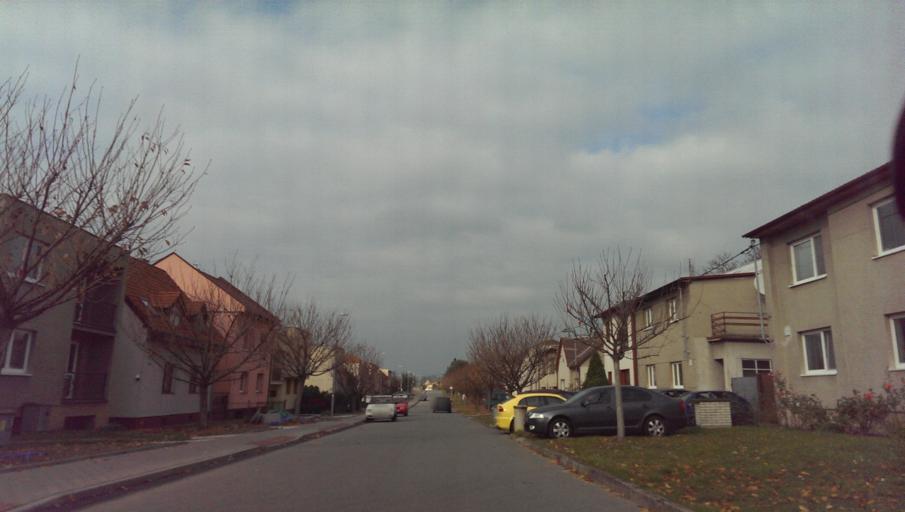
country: CZ
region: Zlin
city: Tlumacov
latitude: 49.2545
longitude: 17.5045
